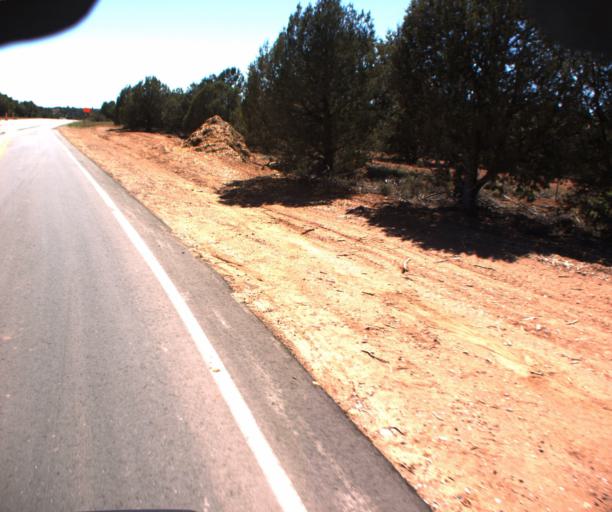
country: US
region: Arizona
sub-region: Yavapai County
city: Paulden
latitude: 34.9869
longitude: -112.3966
